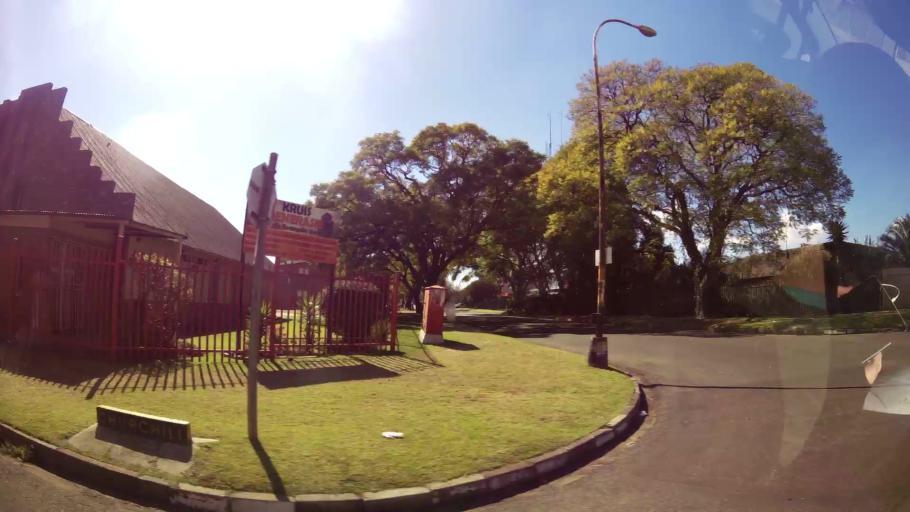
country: ZA
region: Mpumalanga
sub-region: Nkangala District Municipality
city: Witbank
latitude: -25.8853
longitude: 29.2212
